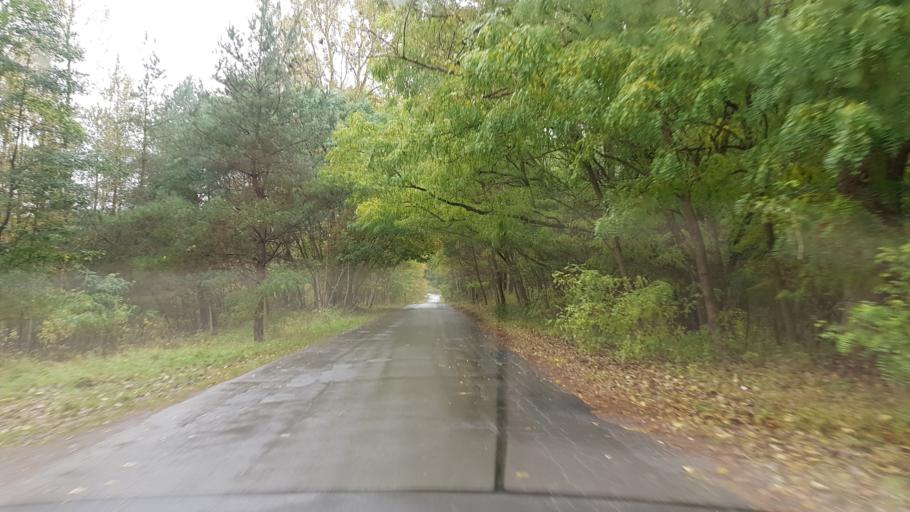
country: PL
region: West Pomeranian Voivodeship
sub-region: Powiat walecki
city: Walcz
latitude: 53.3851
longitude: 16.4834
